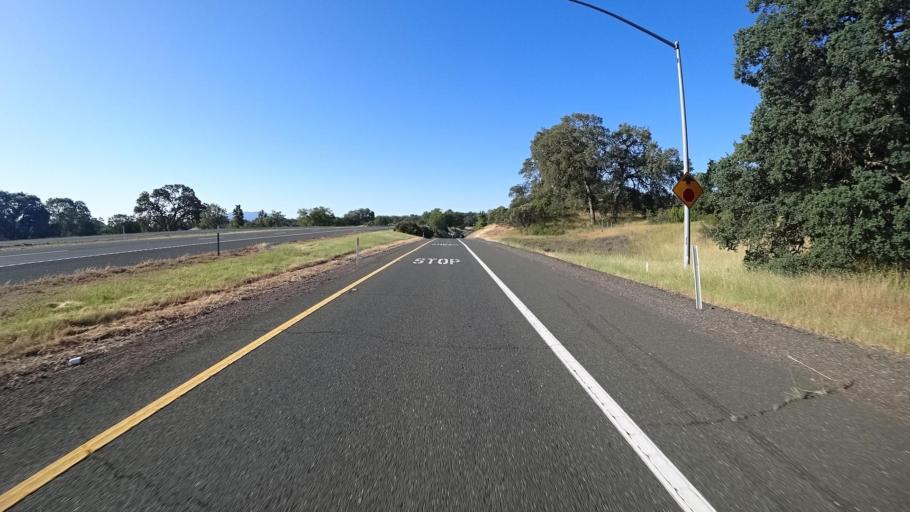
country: US
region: California
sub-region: Lake County
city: North Lakeport
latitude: 39.1204
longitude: -122.9058
